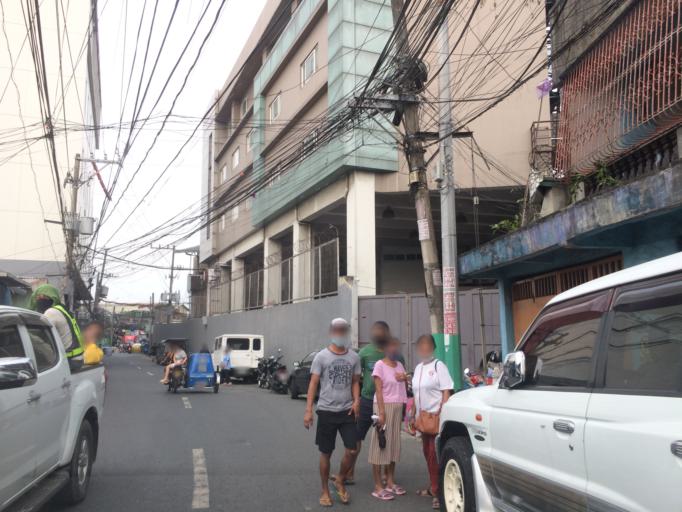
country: PH
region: Calabarzon
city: Bagong Pagasa
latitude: 14.6683
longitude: 121.0112
